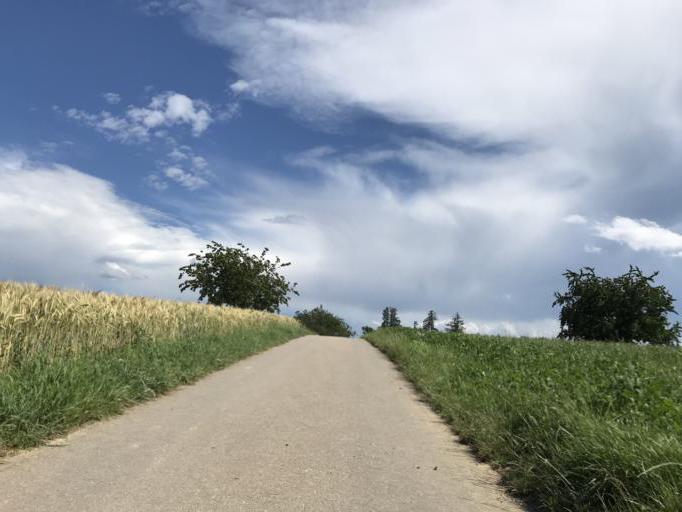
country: DE
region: Baden-Wuerttemberg
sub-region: Freiburg Region
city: Schopfheim
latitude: 47.6315
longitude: 7.8311
